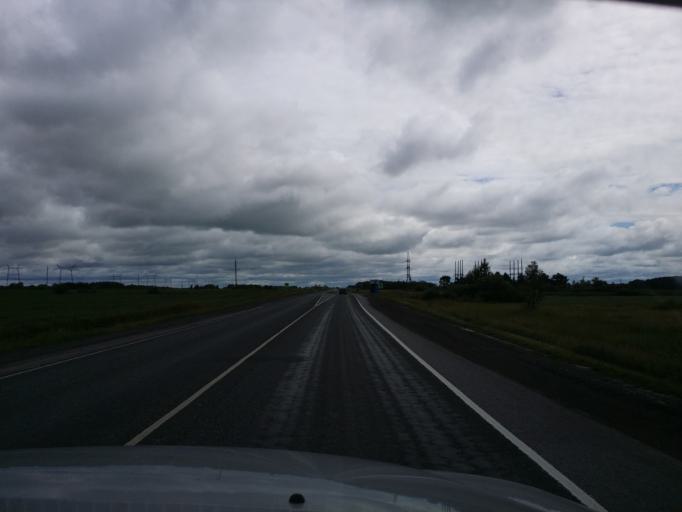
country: RU
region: Tjumen
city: Yarkovo
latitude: 57.1819
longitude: 66.5864
